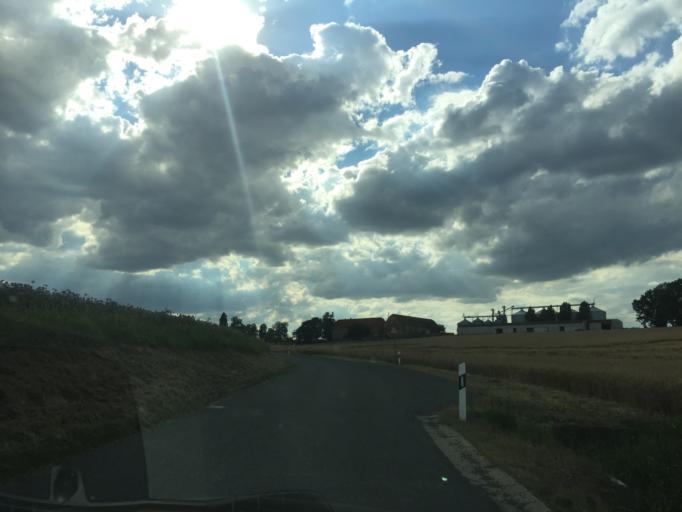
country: DE
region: Thuringia
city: Saara
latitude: 50.9430
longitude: 12.4087
